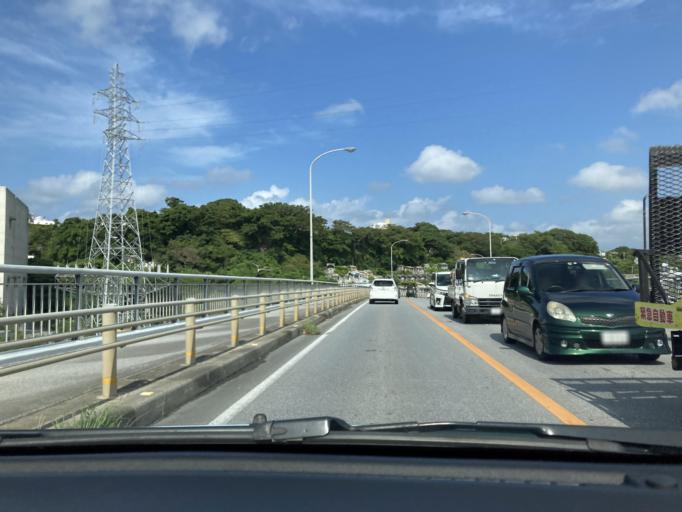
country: JP
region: Okinawa
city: Chatan
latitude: 26.2893
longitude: 127.7859
